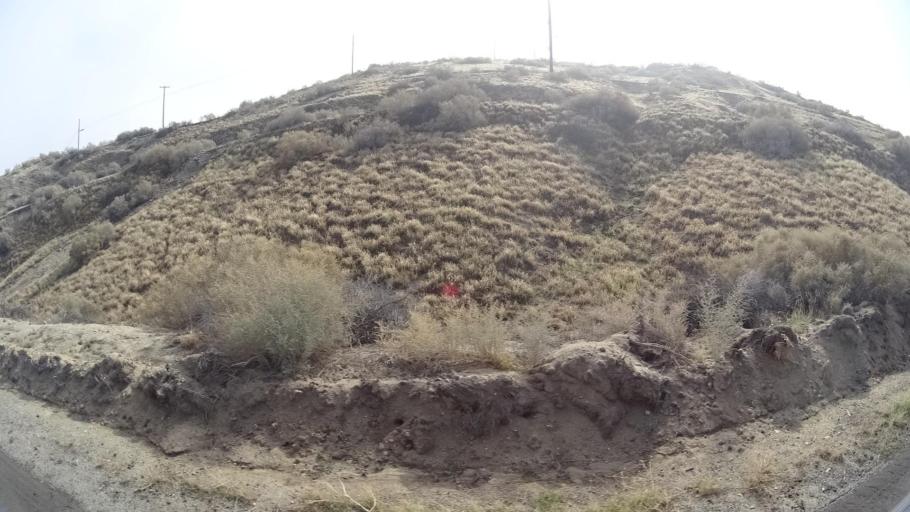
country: US
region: California
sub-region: Kern County
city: Ford City
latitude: 35.1665
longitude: -119.4094
